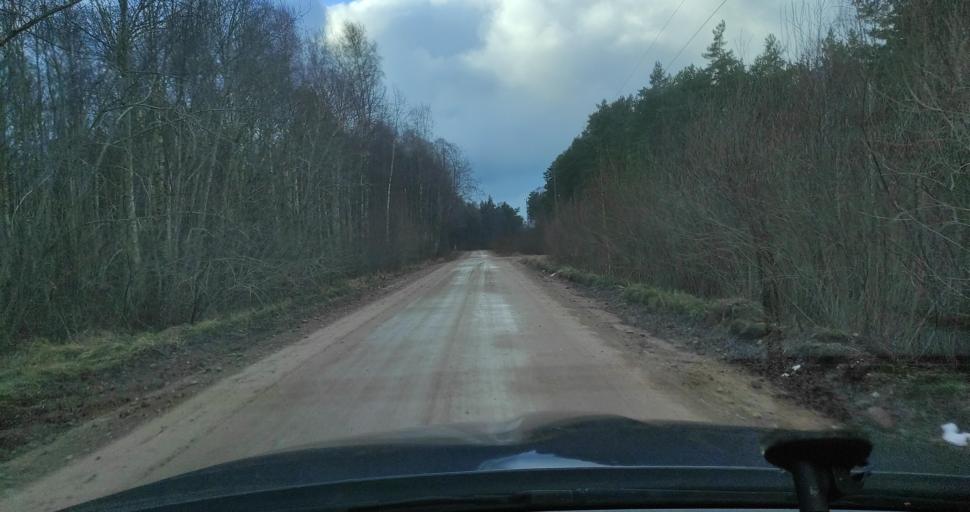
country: LV
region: Pavilostas
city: Pavilosta
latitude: 56.8562
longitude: 21.1419
